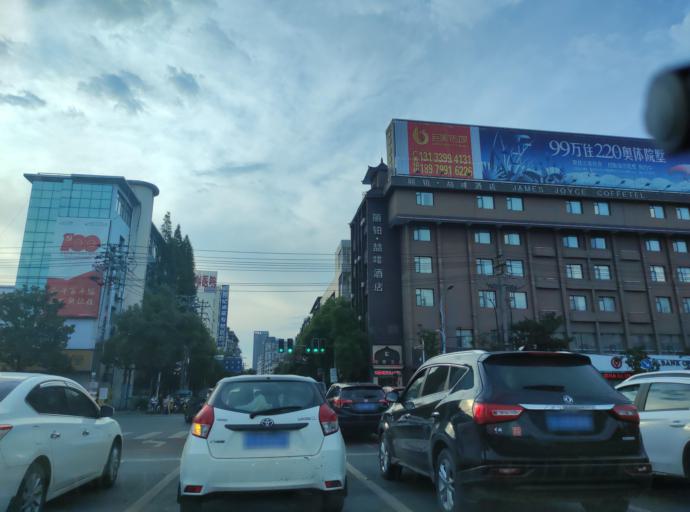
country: CN
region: Jiangxi Sheng
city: Pingxiang
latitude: 27.6349
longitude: 113.8572
